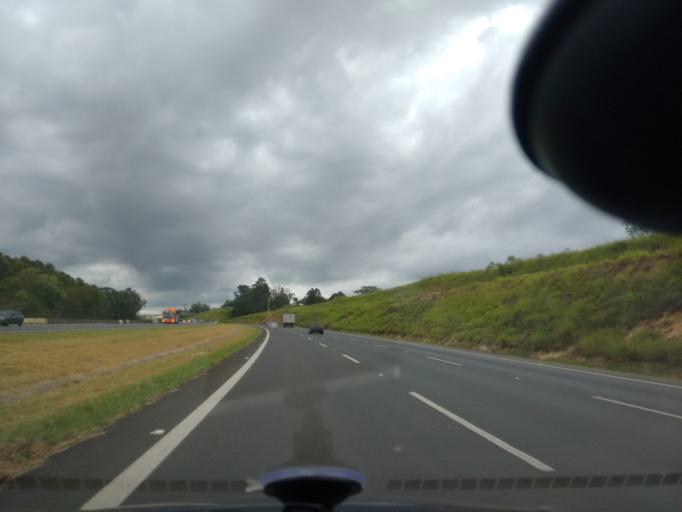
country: BR
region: Sao Paulo
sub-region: Hortolandia
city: Hortolandia
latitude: -22.9112
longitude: -47.1664
